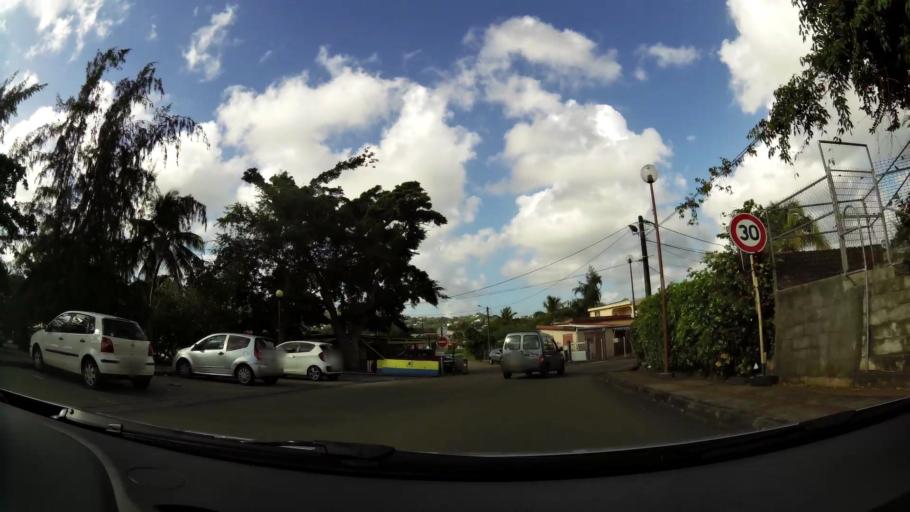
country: MQ
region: Martinique
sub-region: Martinique
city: Le Robert
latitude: 14.6754
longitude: -60.9397
